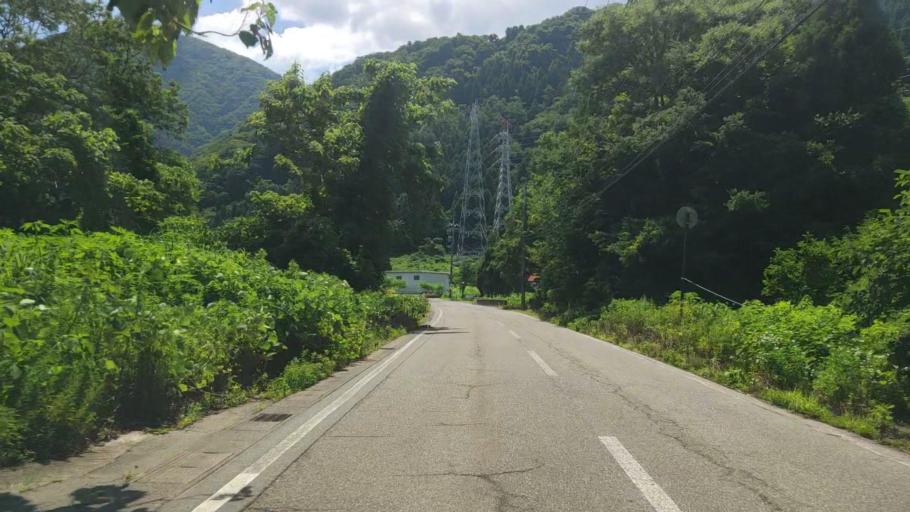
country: JP
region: Fukui
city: Ono
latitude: 35.9368
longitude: 136.5529
